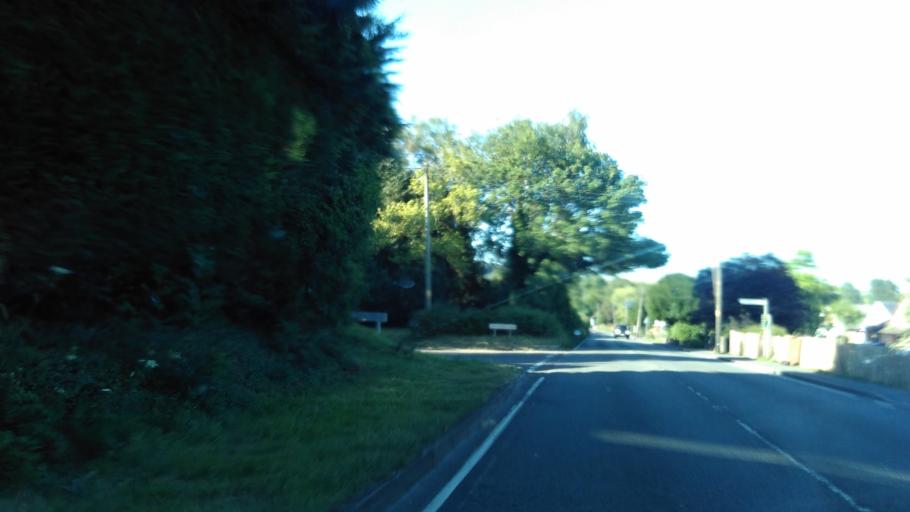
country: GB
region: England
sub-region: Kent
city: Chartham
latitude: 51.2526
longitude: 0.9901
